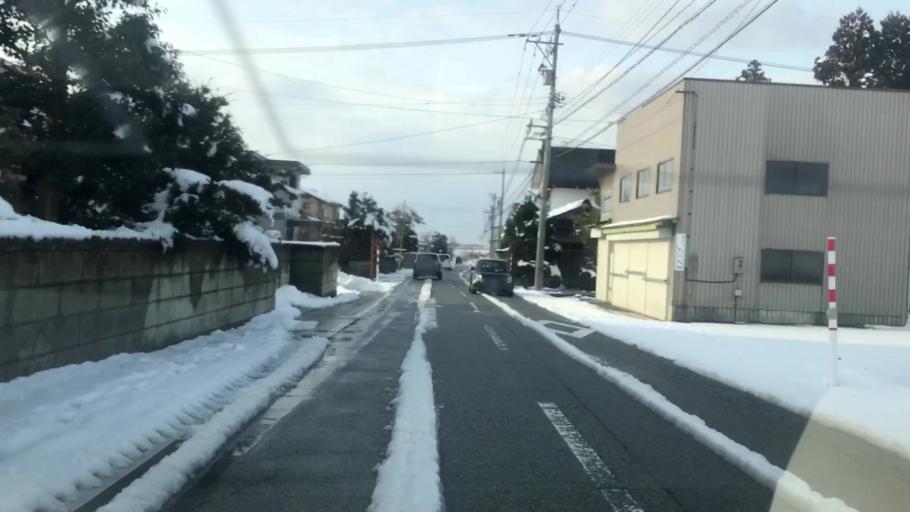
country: JP
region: Toyama
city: Toyama-shi
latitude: 36.6468
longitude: 137.2495
